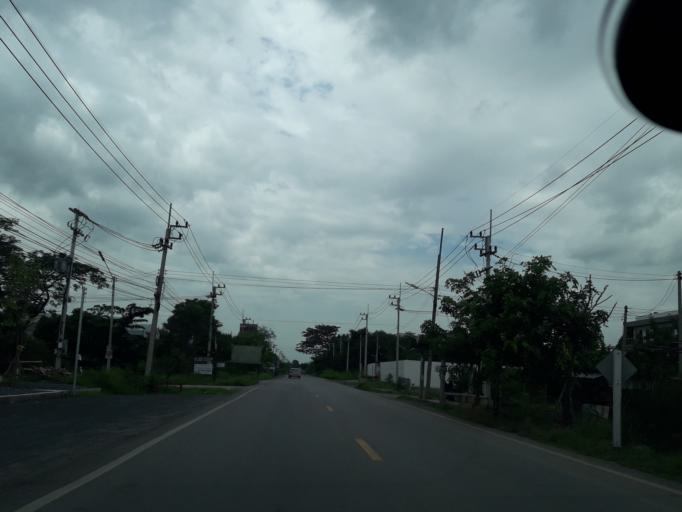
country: TH
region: Pathum Thani
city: Nong Suea
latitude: 14.1318
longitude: 100.7448
